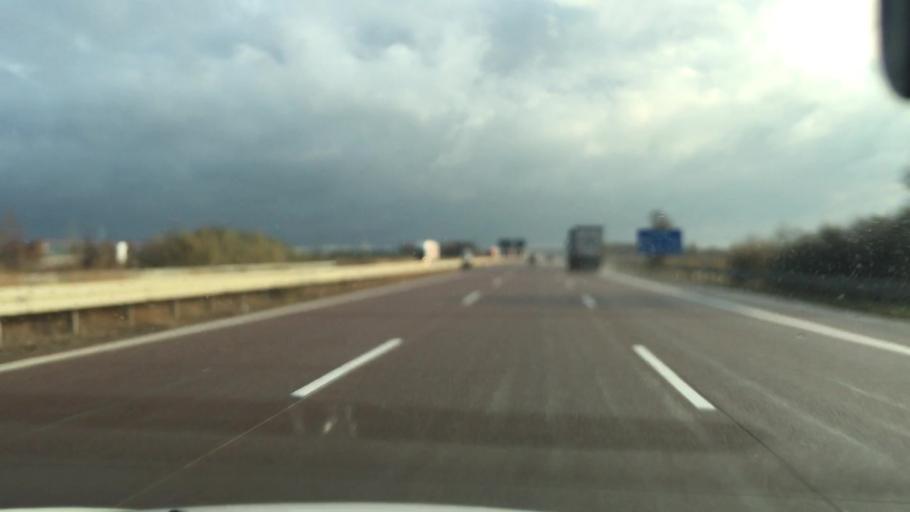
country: DE
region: Saxony-Anhalt
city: Peissen
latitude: 51.4962
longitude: 12.0556
